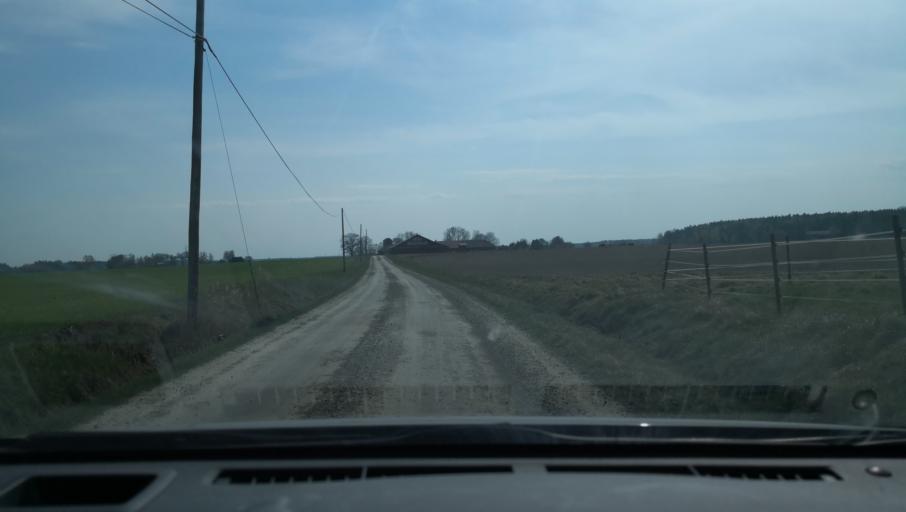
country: SE
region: Vaestmanland
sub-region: Vasteras
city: Skultuna
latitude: 59.8011
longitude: 16.4348
